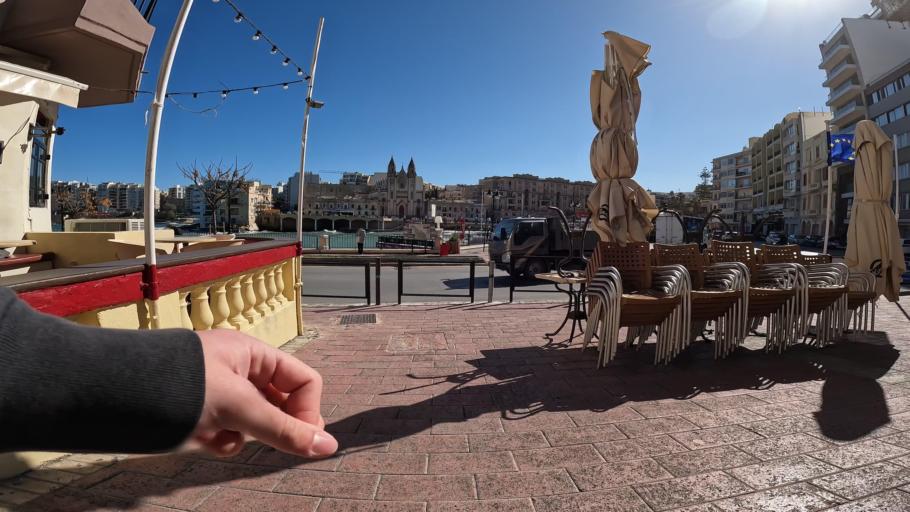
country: MT
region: Saint Julian
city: San Giljan
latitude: 35.9133
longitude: 14.4906
